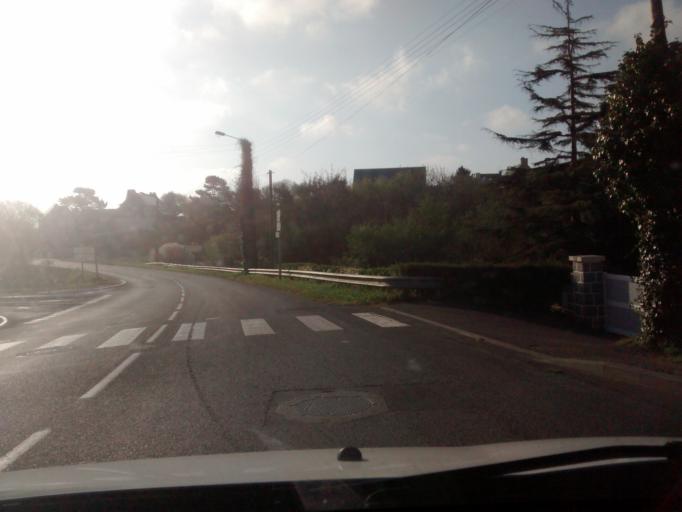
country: FR
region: Brittany
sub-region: Departement des Cotes-d'Armor
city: Perros-Guirec
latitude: 48.8144
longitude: -3.4678
